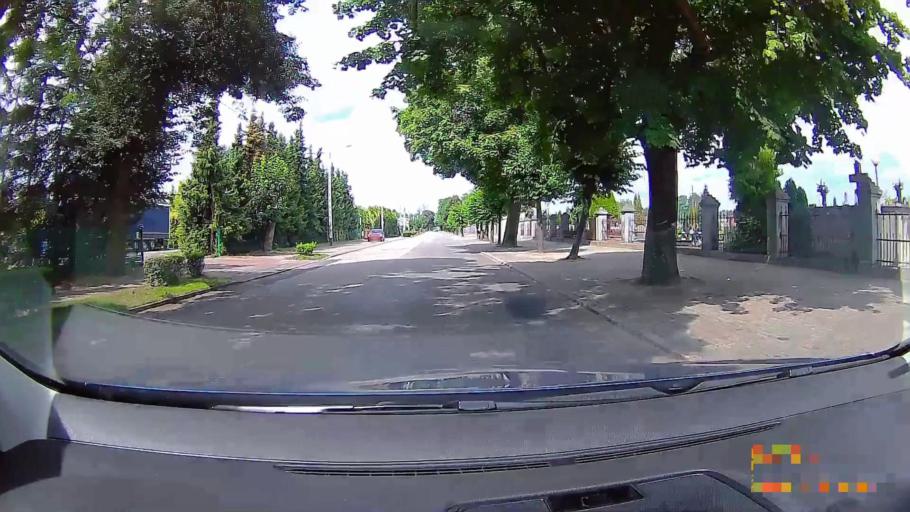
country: PL
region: Greater Poland Voivodeship
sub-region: Powiat koninski
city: Rychwal
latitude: 52.0742
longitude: 18.1630
